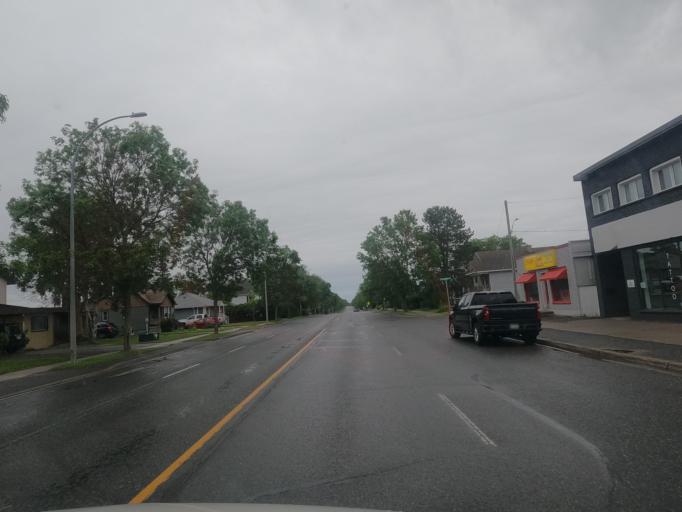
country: CA
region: Ontario
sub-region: Thunder Bay District
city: Thunder Bay
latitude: 48.4674
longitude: -89.1823
